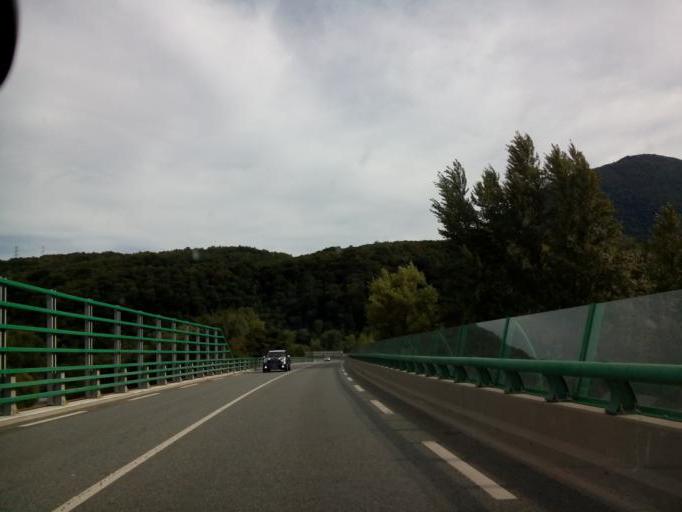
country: FR
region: Rhone-Alpes
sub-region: Departement de l'Isere
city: Champ-sur-Drac
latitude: 45.0849
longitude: 5.7384
